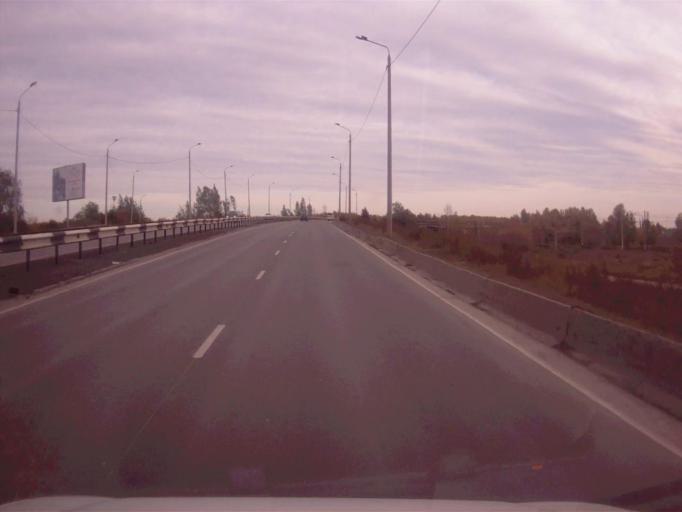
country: RU
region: Chelyabinsk
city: Novosineglazovskiy
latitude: 55.0411
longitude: 61.4350
